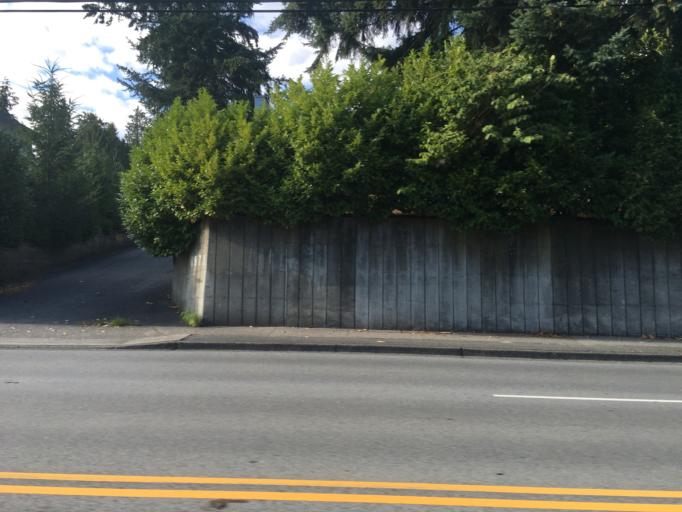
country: CA
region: British Columbia
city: Port Moody
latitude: 49.2489
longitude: -122.8422
